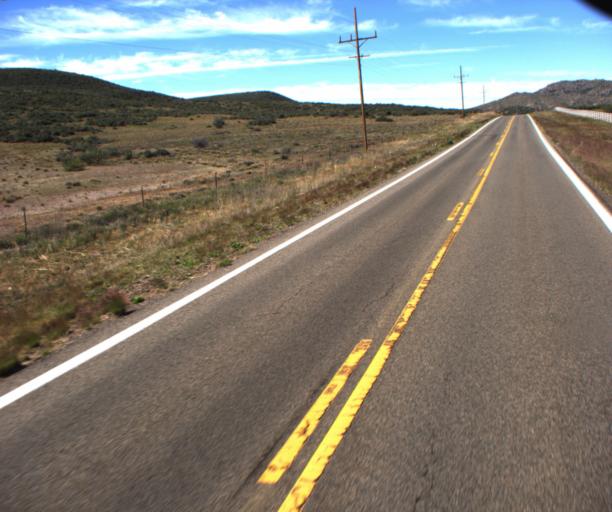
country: US
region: Arizona
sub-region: Yavapai County
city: Congress
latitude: 34.2578
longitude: -112.7311
